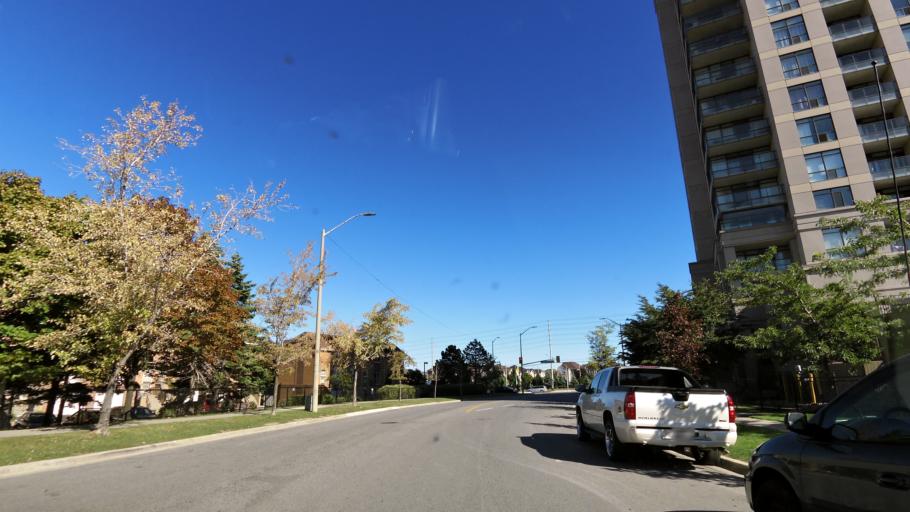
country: CA
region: Ontario
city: Mississauga
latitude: 43.6117
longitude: -79.6491
